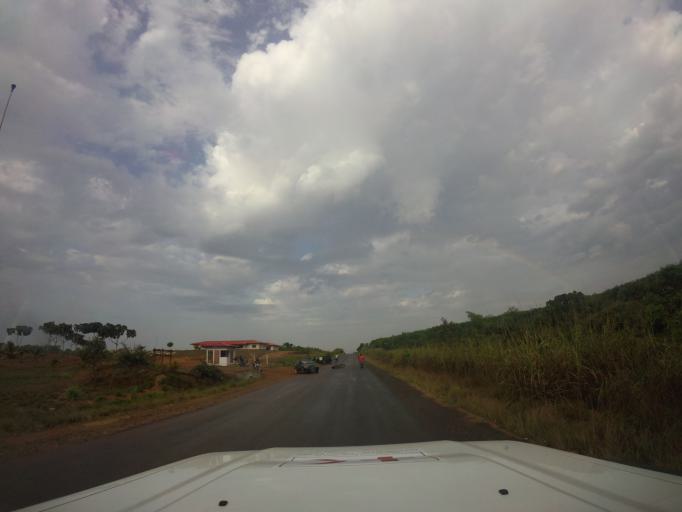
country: LR
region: Bomi
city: Tubmanburg
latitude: 6.7302
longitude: -11.0131
